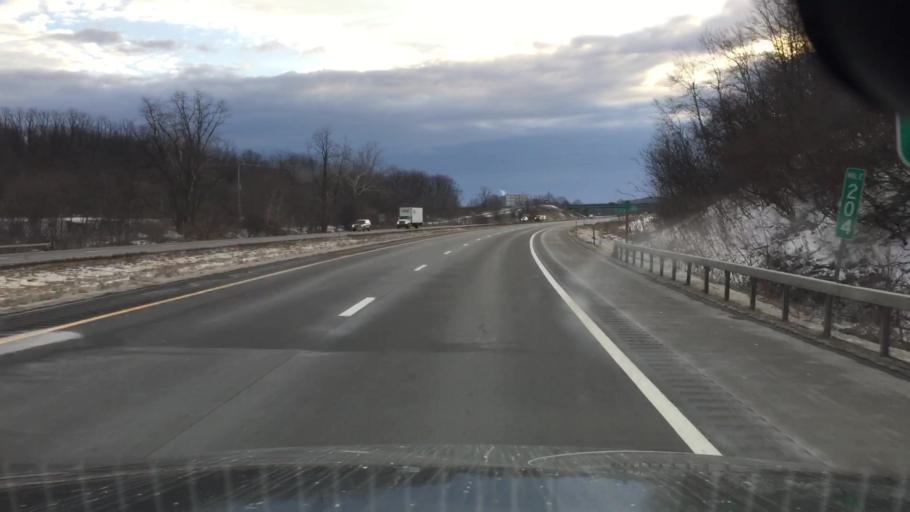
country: US
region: Pennsylvania
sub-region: Bradford County
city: South Waverly
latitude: 42.0004
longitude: -76.5557
